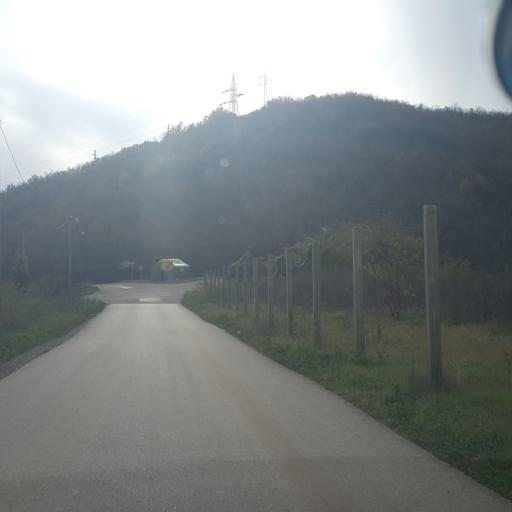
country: RS
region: Central Serbia
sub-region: Zajecarski Okrug
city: Knjazevac
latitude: 43.5824
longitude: 22.2482
